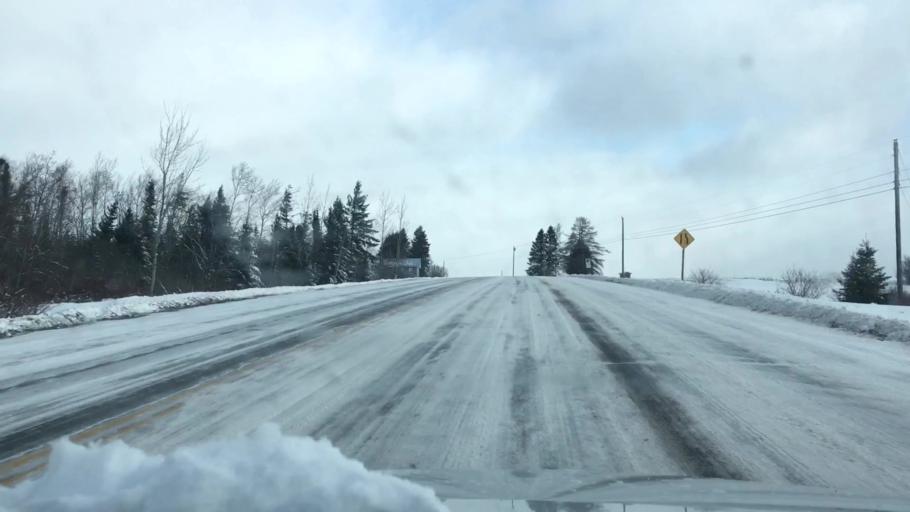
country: US
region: Maine
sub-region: Aroostook County
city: Van Buren
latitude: 47.0972
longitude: -67.9768
